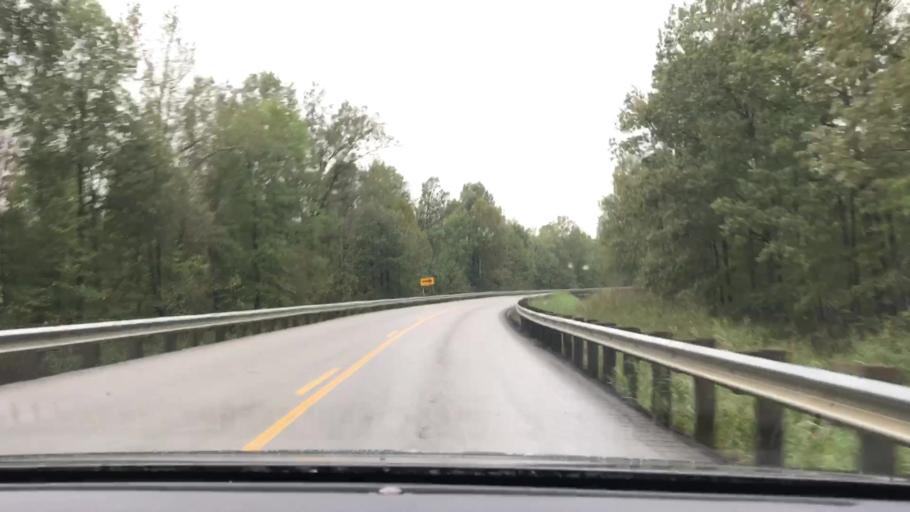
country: US
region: Kentucky
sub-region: McLean County
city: Calhoun
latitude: 37.3946
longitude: -87.2998
